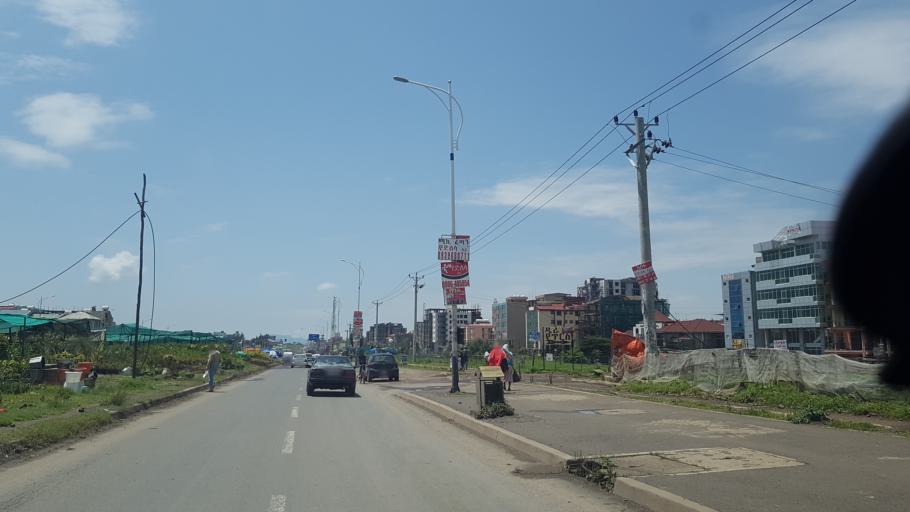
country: ET
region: Adis Abeba
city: Addis Ababa
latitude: 9.0128
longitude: 38.8520
